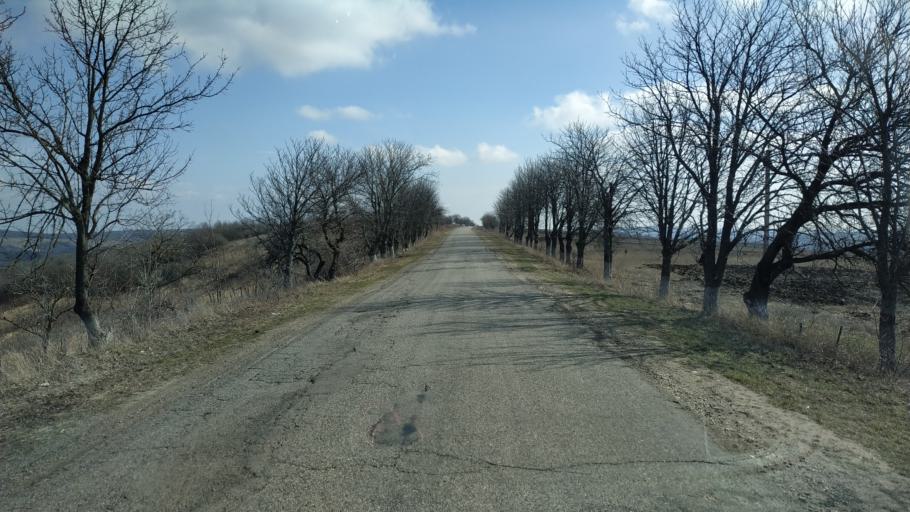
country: MD
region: Hincesti
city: Hincesti
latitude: 46.8530
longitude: 28.6441
